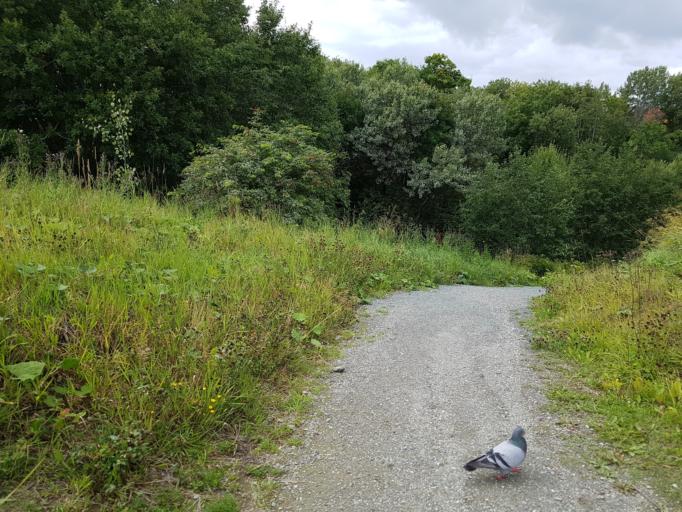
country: NO
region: Sor-Trondelag
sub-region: Trondheim
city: Trondheim
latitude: 63.4230
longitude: 10.4604
